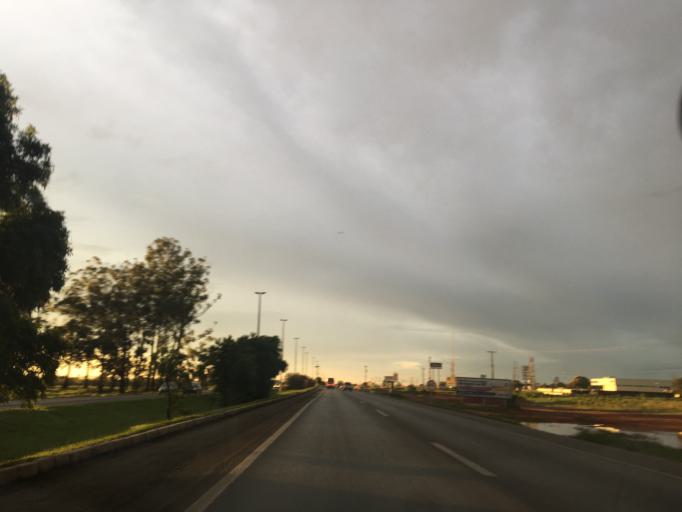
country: BR
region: Goias
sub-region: Luziania
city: Luziania
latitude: -16.0153
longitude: -47.9816
